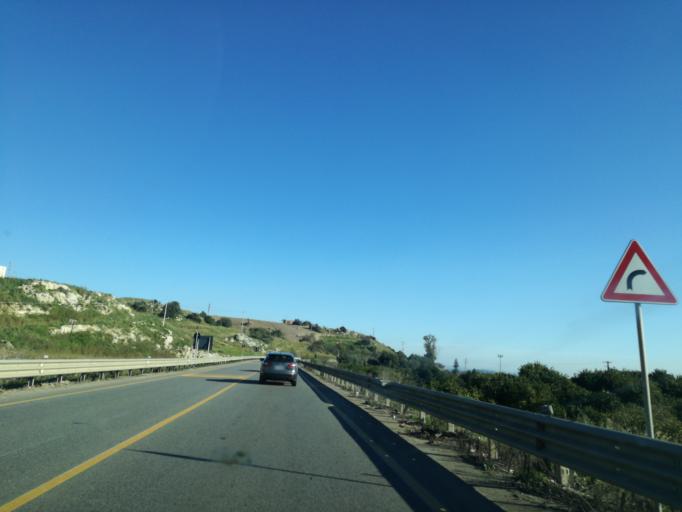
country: IT
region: Sicily
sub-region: Catania
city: Ramacca
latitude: 37.3621
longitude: 14.7135
